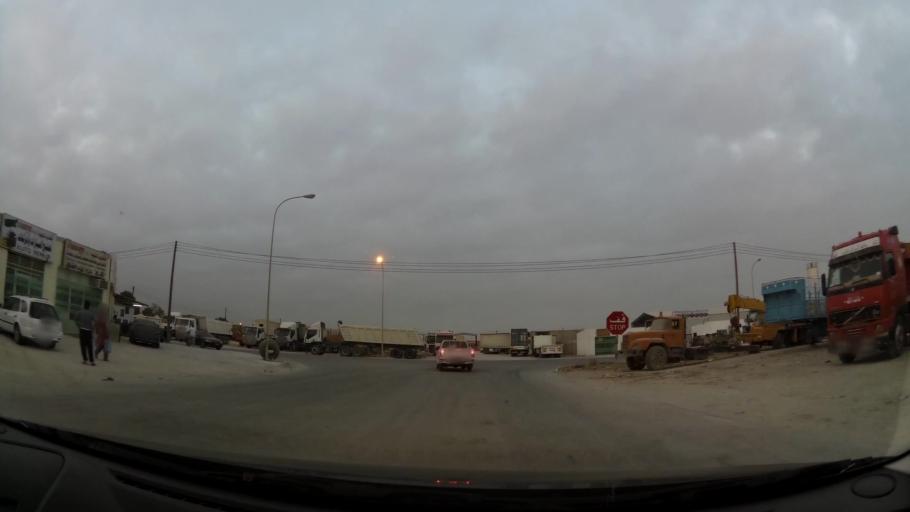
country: OM
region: Zufar
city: Salalah
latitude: 17.0274
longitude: 54.0388
